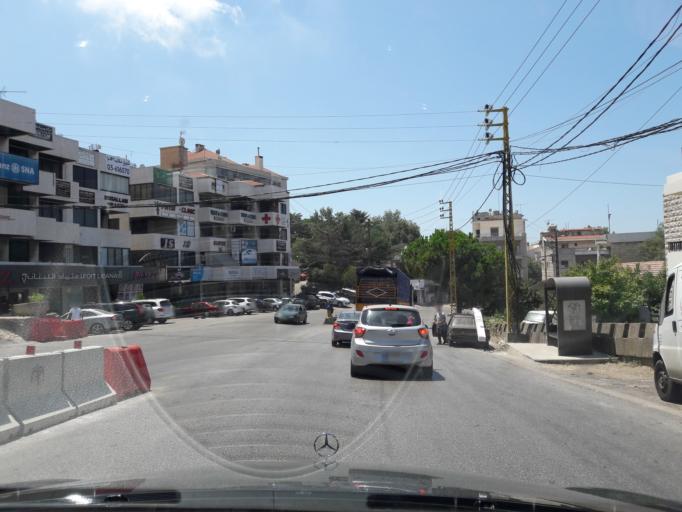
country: LB
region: Mont-Liban
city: Djounie
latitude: 33.9208
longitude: 35.6302
